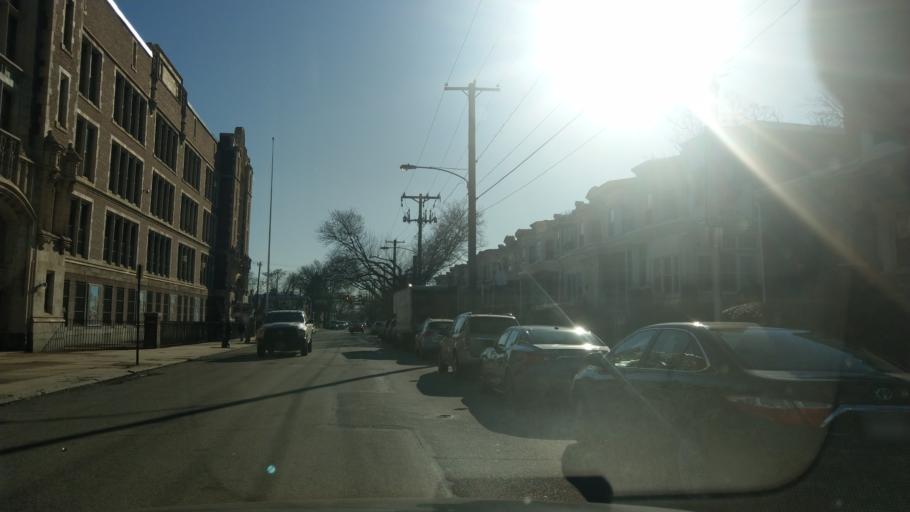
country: US
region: Pennsylvania
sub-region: Montgomery County
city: Wyncote
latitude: 40.0542
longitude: -75.1528
